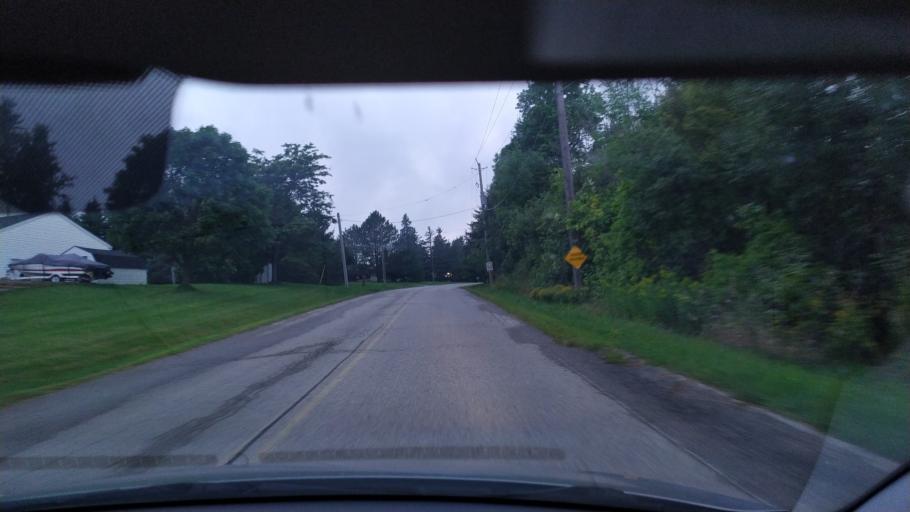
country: CA
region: Ontario
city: Kitchener
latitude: 43.3547
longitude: -80.6677
